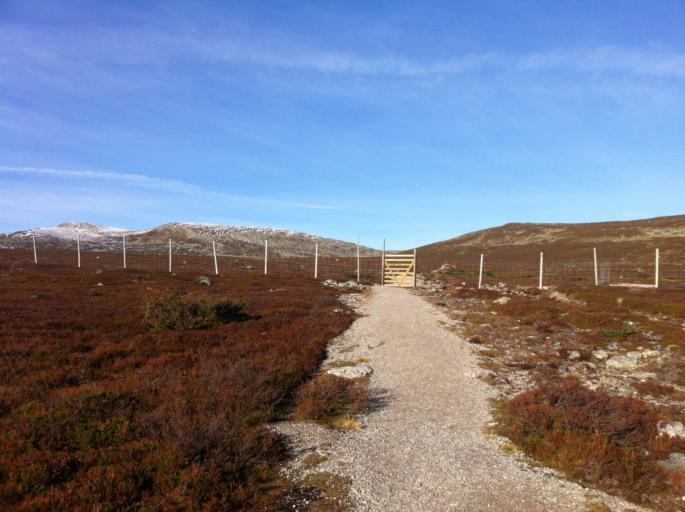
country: NO
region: Hedmark
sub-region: Engerdal
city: Engerdal
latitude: 62.1166
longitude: 12.2617
